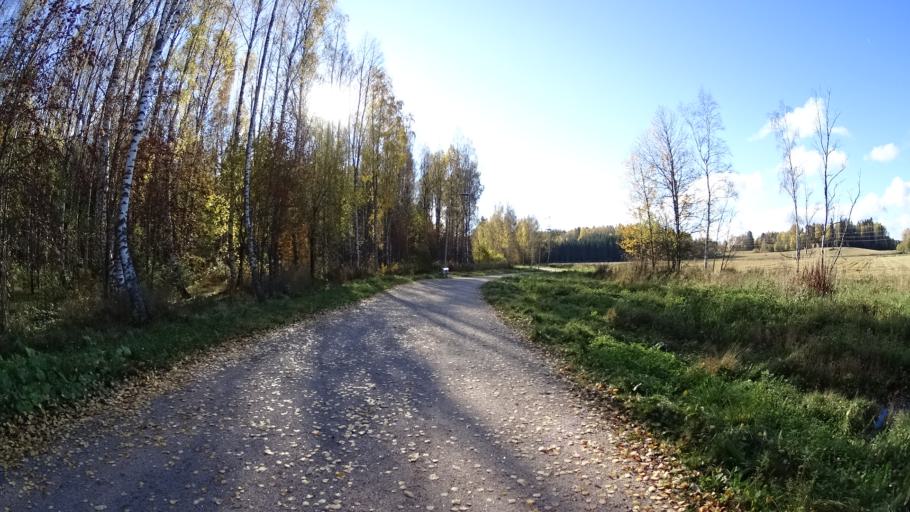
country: FI
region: Uusimaa
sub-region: Helsinki
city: Kilo
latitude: 60.2388
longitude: 24.7967
